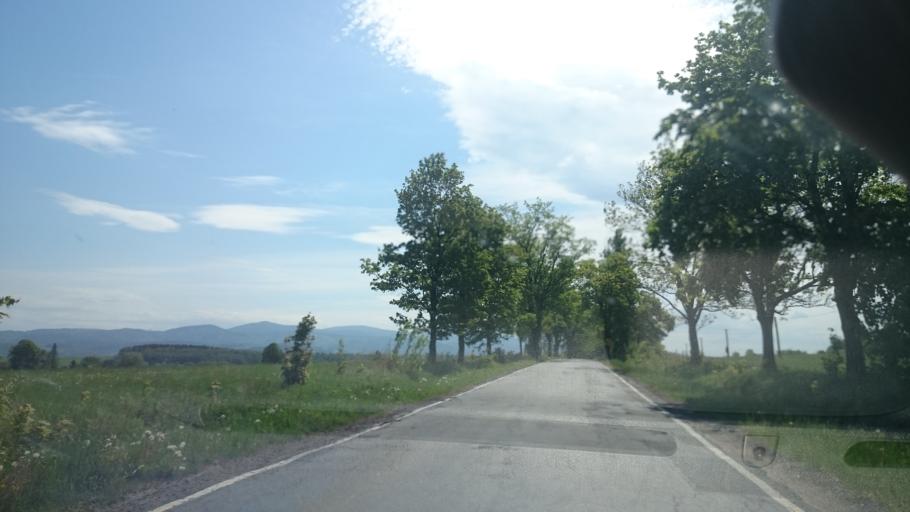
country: PL
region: Lower Silesian Voivodeship
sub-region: Powiat klodzki
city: Bystrzyca Klodzka
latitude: 50.3289
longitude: 16.6044
